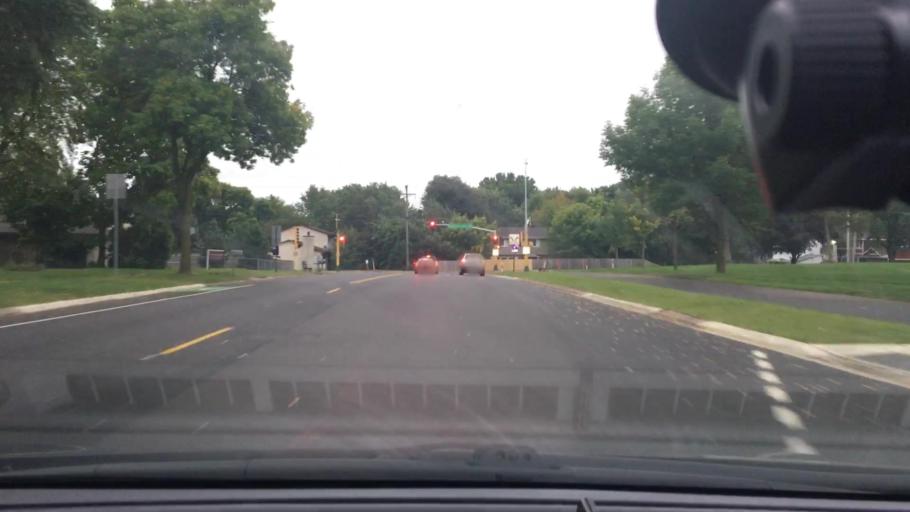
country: US
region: Minnesota
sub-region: Hennepin County
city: New Hope
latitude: 45.0083
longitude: -93.3904
